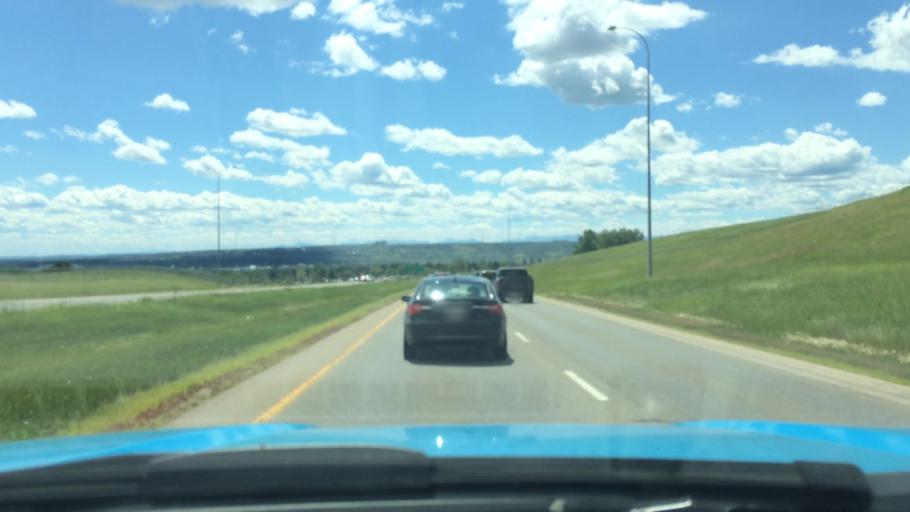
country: CA
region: Alberta
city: Calgary
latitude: 51.1137
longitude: -114.1360
